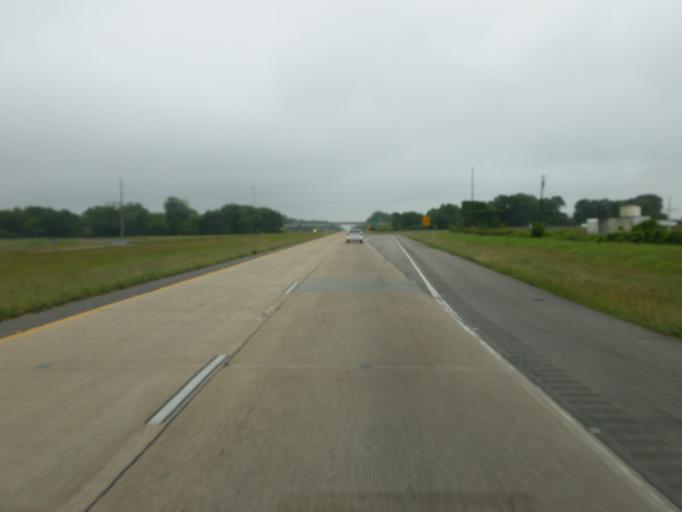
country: US
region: Louisiana
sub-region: Madison Parish
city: Tallulah
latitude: 32.3821
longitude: -91.1775
